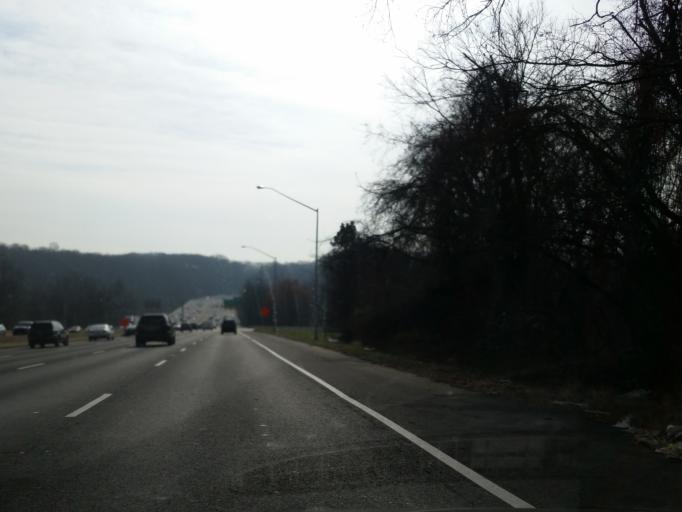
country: US
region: Maryland
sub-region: Montgomery County
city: Cabin John
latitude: 38.9743
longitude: -77.1788
